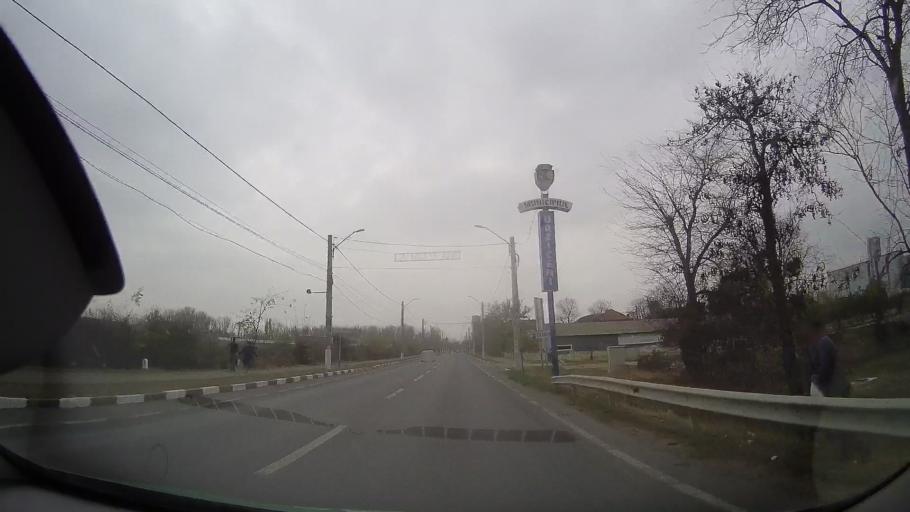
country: RO
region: Ialomita
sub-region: Comuna Manasia
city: Manasia
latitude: 44.7118
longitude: 26.6602
